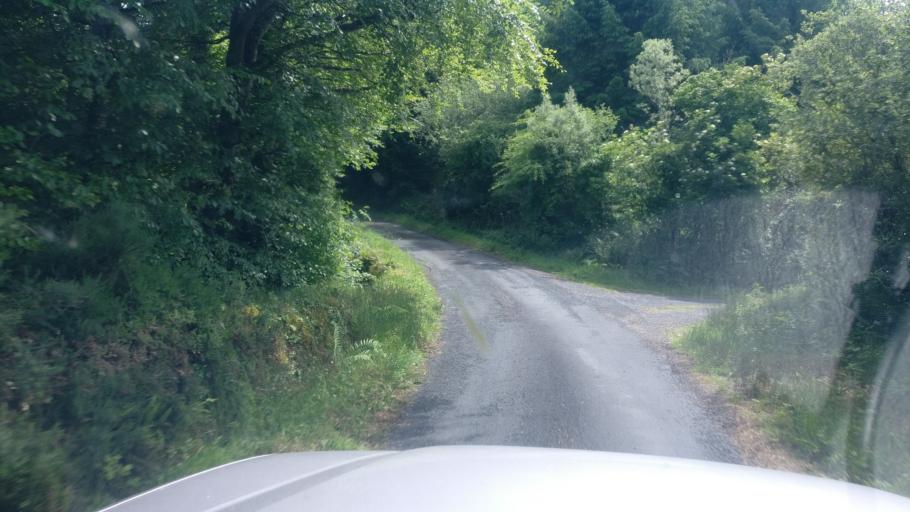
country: IE
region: Connaught
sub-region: County Galway
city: Gort
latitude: 53.0803
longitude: -8.7099
